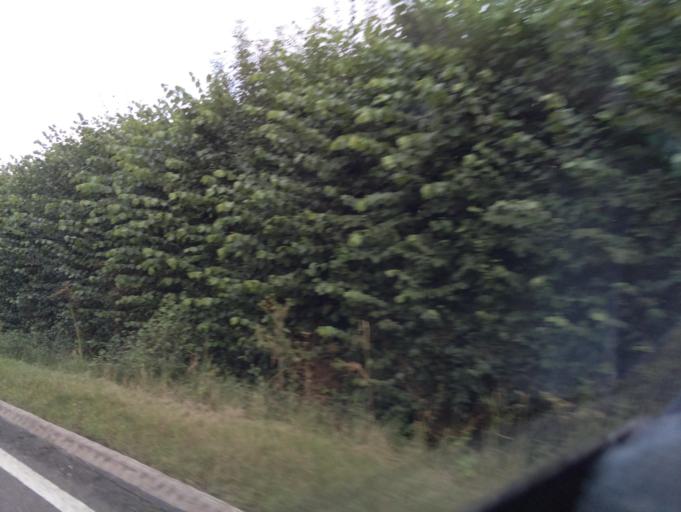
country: GB
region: England
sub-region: Warwickshire
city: Southam
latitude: 52.2703
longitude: -1.3706
